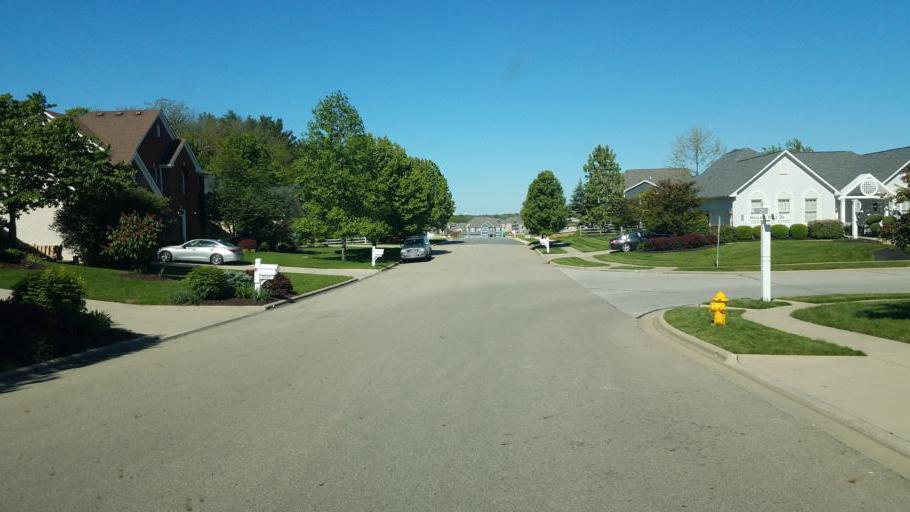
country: US
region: Ohio
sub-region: Franklin County
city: Westerville
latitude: 40.1735
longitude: -82.9417
